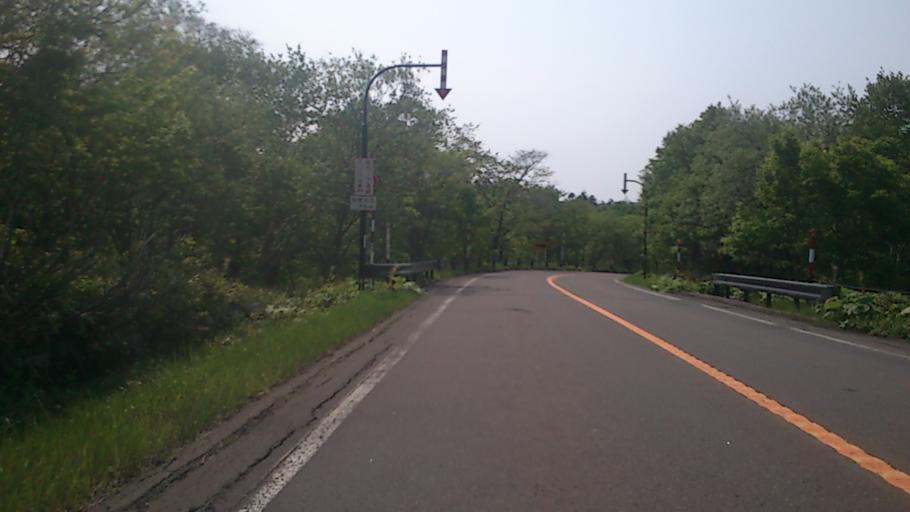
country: JP
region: Hokkaido
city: Bihoro
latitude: 43.5430
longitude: 144.5073
